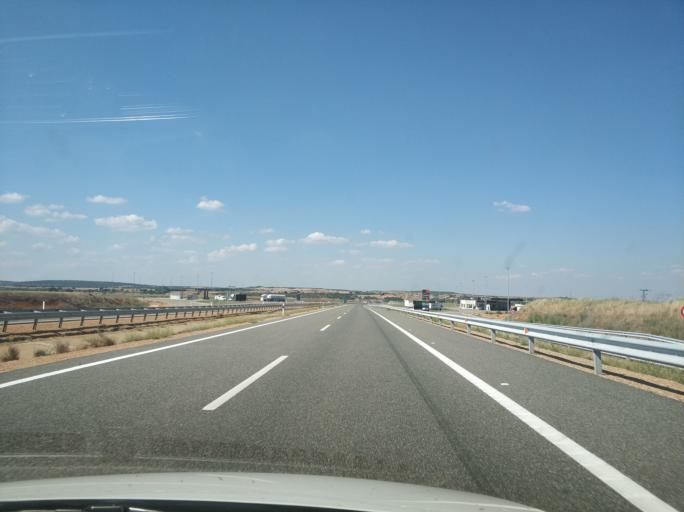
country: ES
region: Castille and Leon
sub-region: Provincia de Zamora
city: Granja de Moreruela
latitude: 41.7965
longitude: -5.7568
